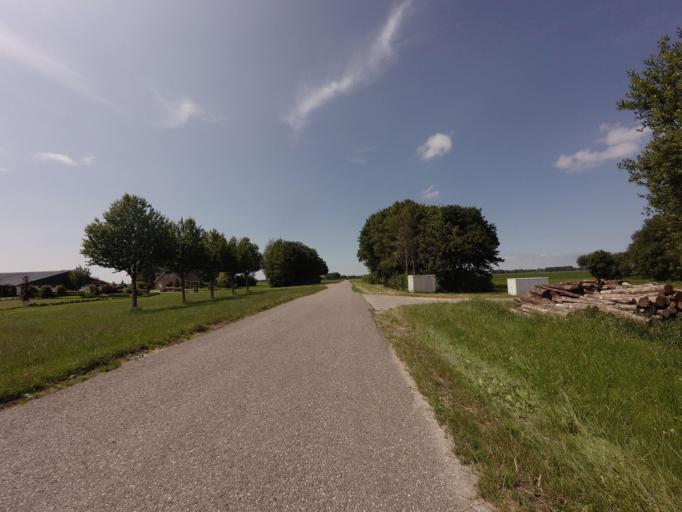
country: NL
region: Flevoland
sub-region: Gemeente Lelystad
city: Lelystad
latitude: 52.4350
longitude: 5.4697
